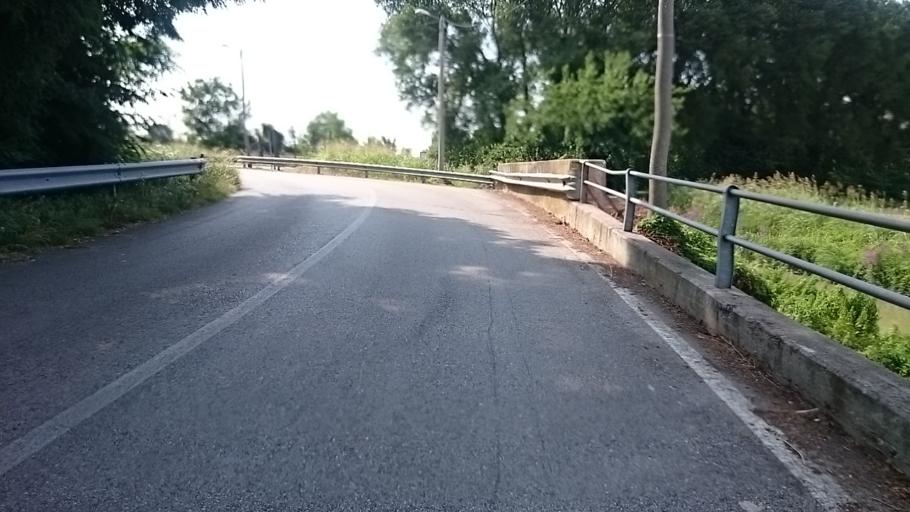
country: IT
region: Veneto
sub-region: Provincia di Venezia
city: Fornase
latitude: 45.4579
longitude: 12.1940
